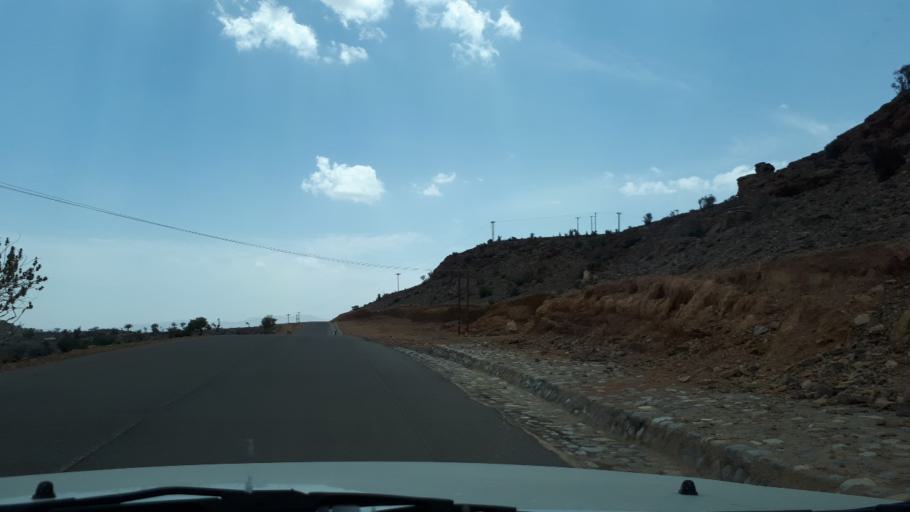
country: OM
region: Muhafazat ad Dakhiliyah
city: Bahla'
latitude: 23.2226
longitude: 57.2049
